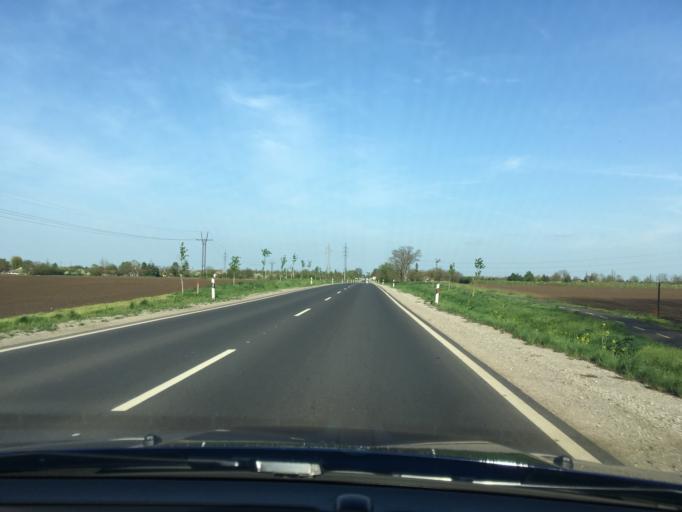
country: HU
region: Bekes
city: Bekescsaba
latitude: 46.6786
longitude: 21.0317
